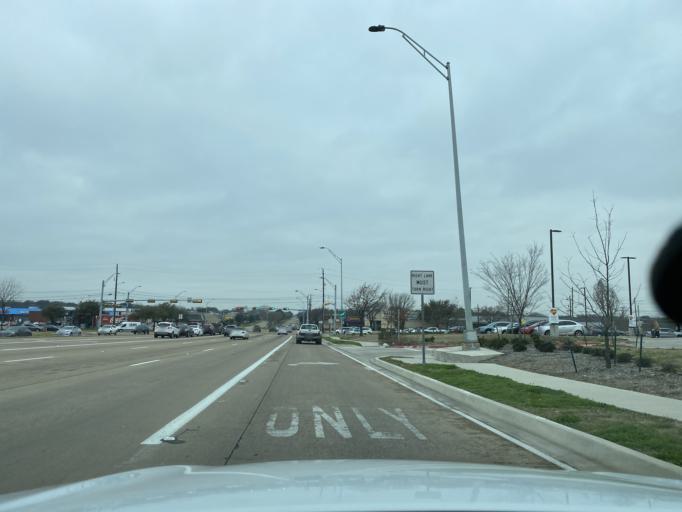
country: US
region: Texas
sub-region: Tarrant County
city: Arlington
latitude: 32.7082
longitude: -97.0964
